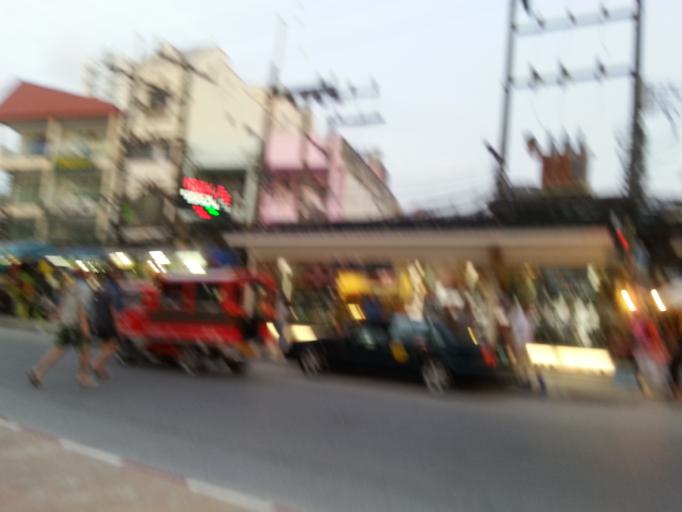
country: TH
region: Phuket
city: Patong
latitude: 7.8904
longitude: 98.2932
